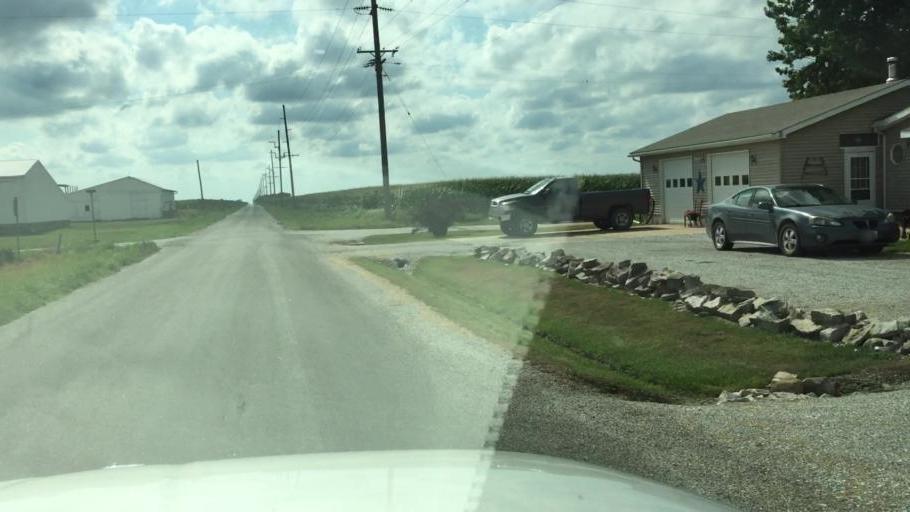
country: US
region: Illinois
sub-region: Hancock County
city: Carthage
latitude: 40.4169
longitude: -91.1779
